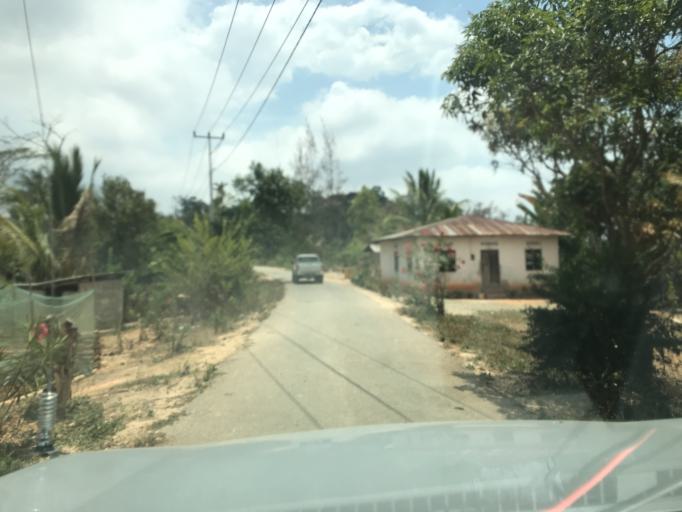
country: TL
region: Dili
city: Dili
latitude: -8.6095
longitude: 125.5743
